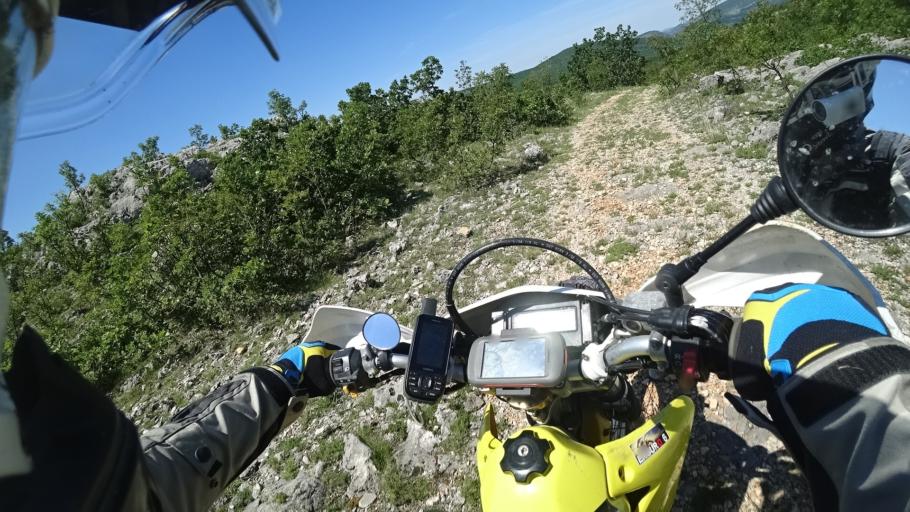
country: BA
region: Federation of Bosnia and Herzegovina
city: Bosansko Grahovo
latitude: 44.0169
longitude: 16.3616
